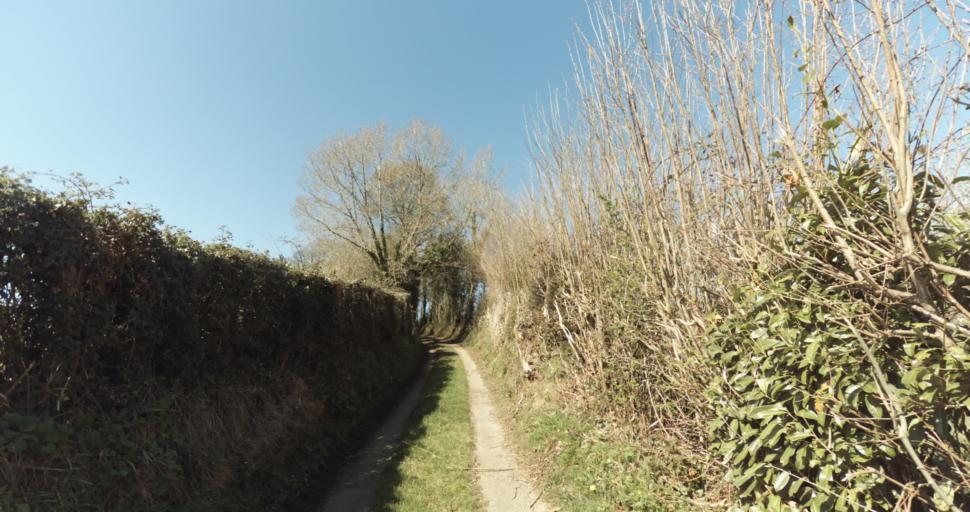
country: FR
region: Lower Normandy
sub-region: Departement du Calvados
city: Livarot
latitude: 48.9957
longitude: 0.0611
